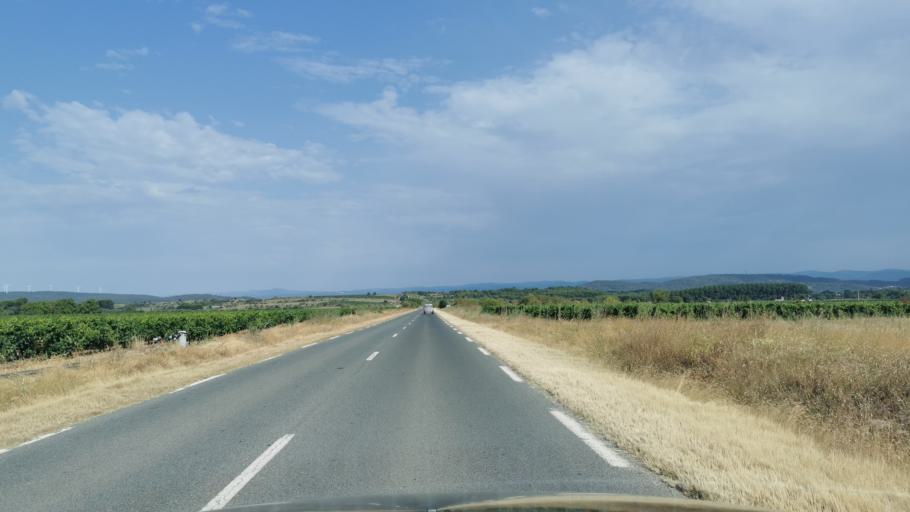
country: FR
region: Languedoc-Roussillon
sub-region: Departement de l'Aude
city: Ginestas
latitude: 43.2818
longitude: 2.8774
